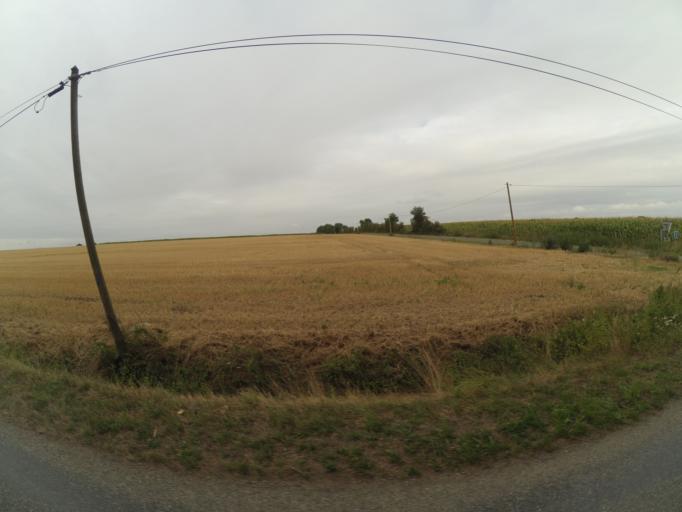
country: FR
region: Pays de la Loire
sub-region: Departement de la Vendee
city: Saint-Andre-Treize-Voies
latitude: 46.9520
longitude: -1.4176
